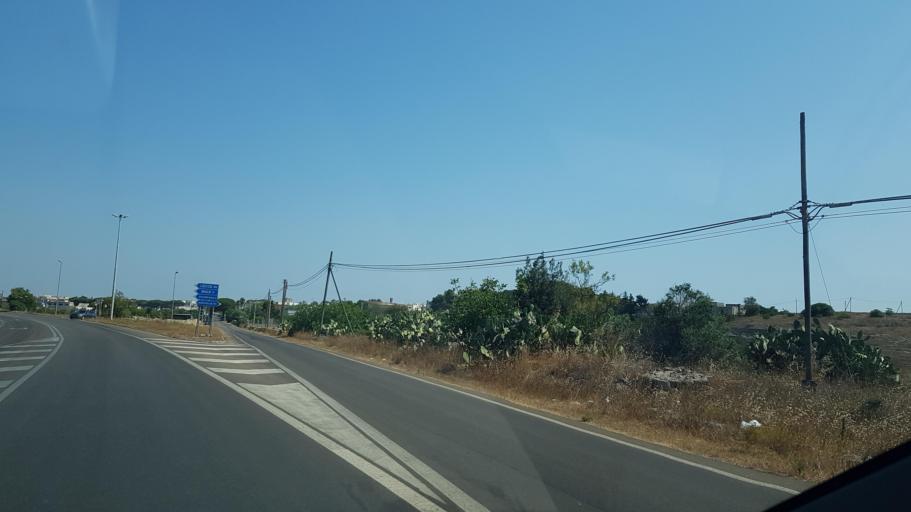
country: IT
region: Apulia
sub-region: Provincia di Lecce
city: Nociglia
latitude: 40.0298
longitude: 18.3250
